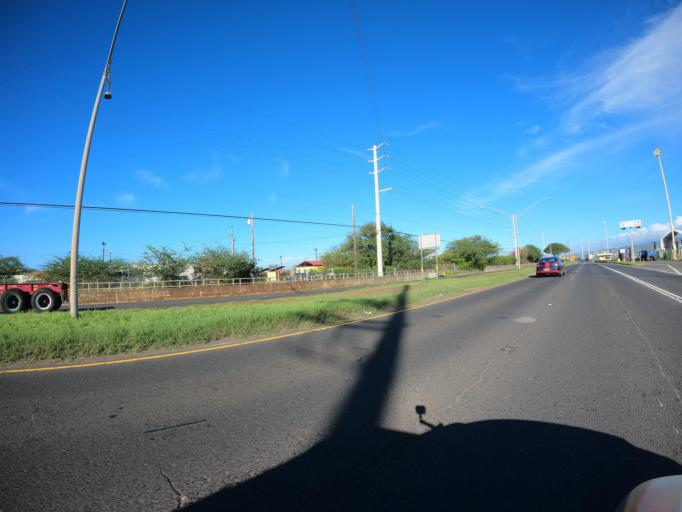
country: US
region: Hawaii
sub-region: Honolulu County
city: Honolulu
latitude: 21.3109
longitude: -157.8864
